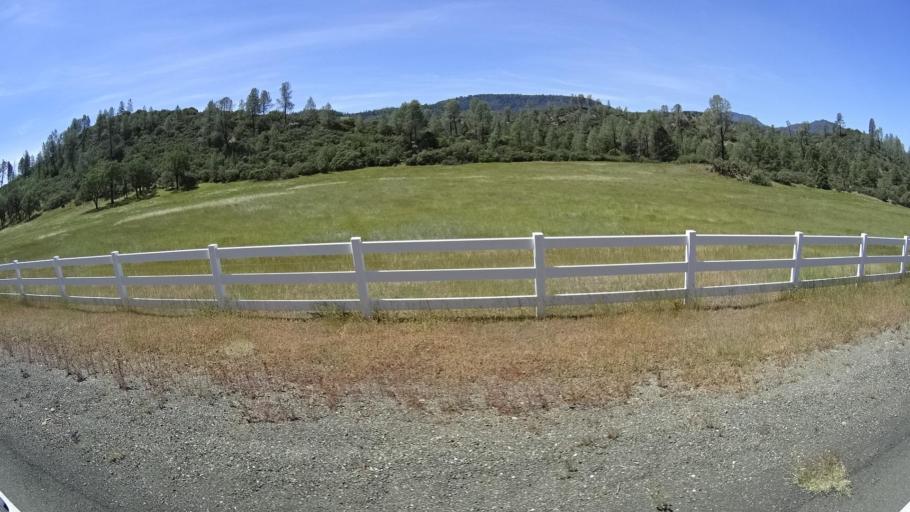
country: US
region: California
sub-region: Lake County
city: Hidden Valley Lake
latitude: 38.7215
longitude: -122.5046
